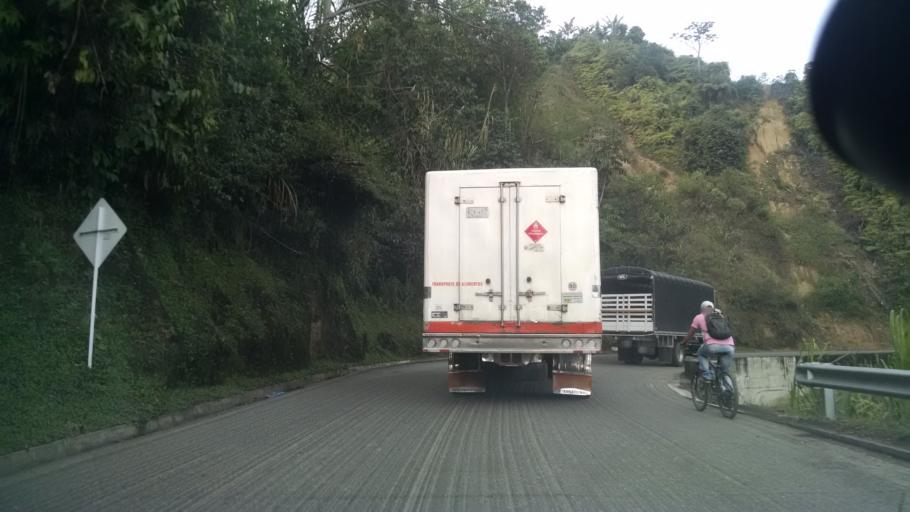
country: CO
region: Antioquia
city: Santa Barbara
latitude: 5.9007
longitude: -75.5740
